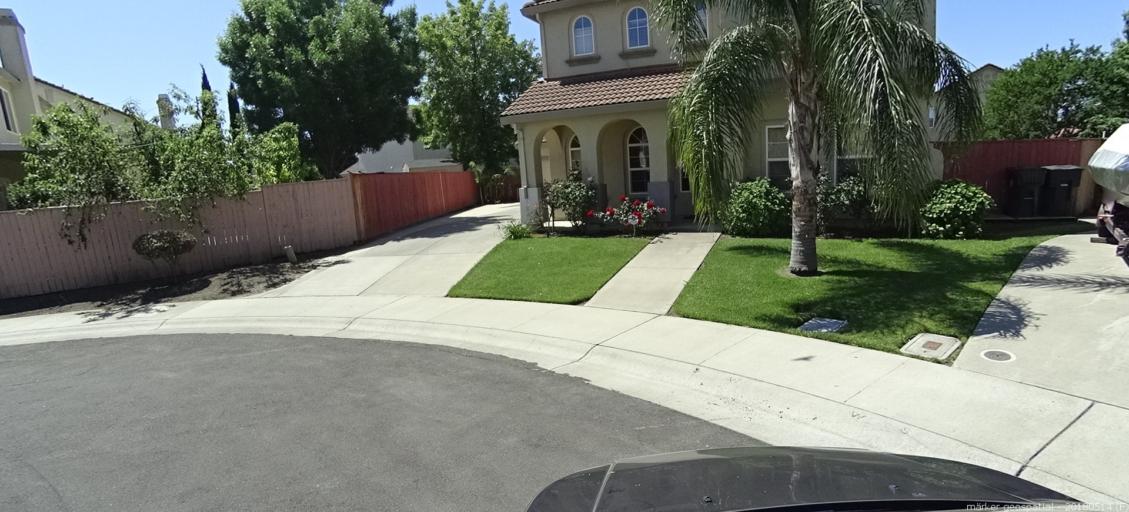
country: US
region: California
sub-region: Yolo County
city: West Sacramento
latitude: 38.6355
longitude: -121.5329
